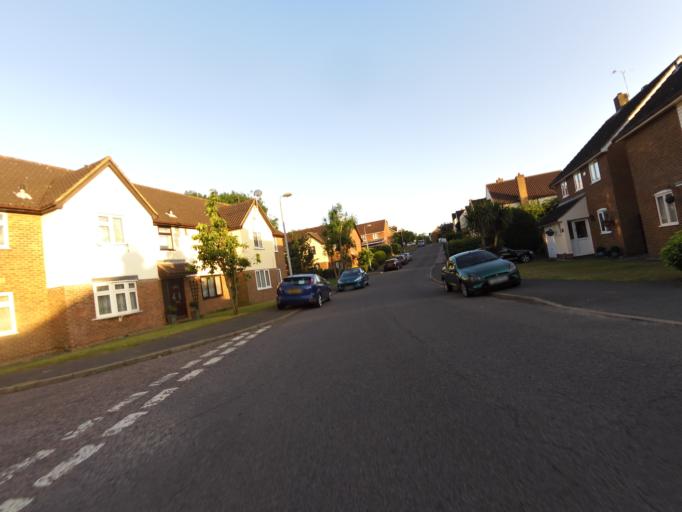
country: GB
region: England
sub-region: Suffolk
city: Kesgrave
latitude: 52.0521
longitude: 1.2149
